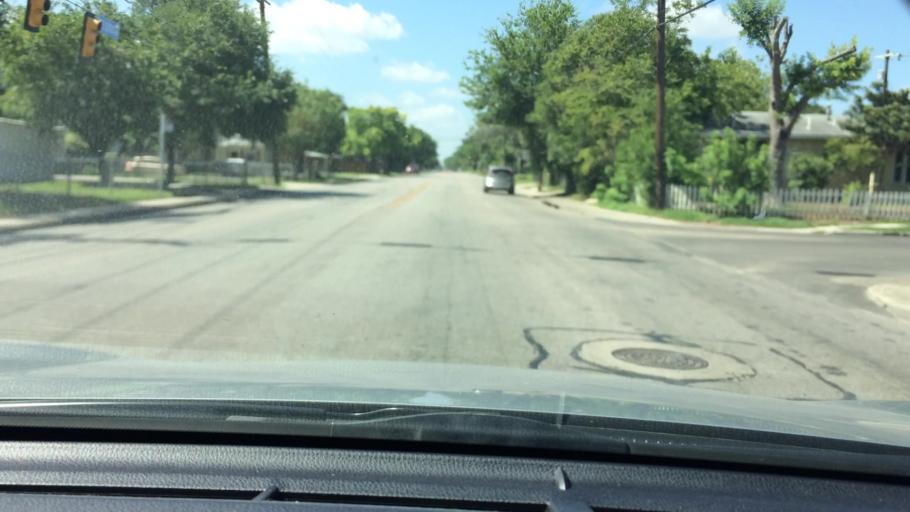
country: US
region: Texas
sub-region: Bexar County
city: Castle Hills
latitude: 29.5073
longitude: -98.5352
